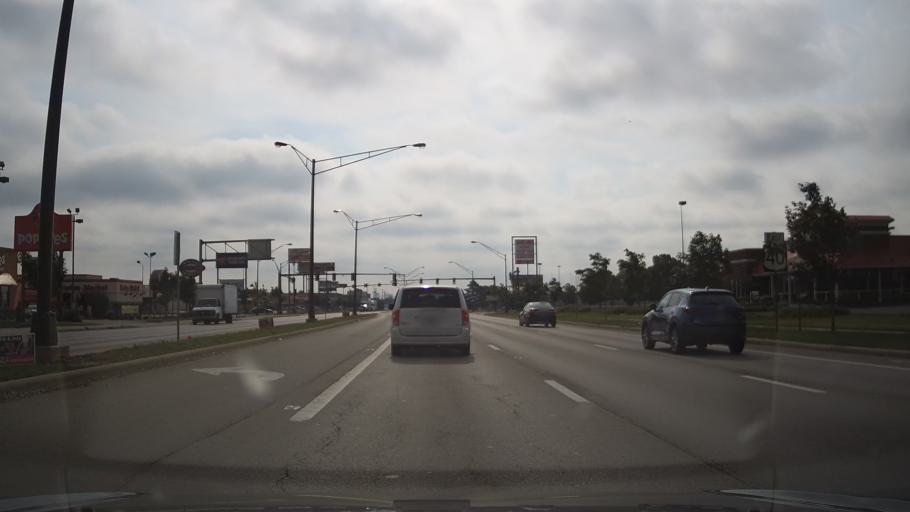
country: US
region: Ohio
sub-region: Franklin County
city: Lincoln Village
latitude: 39.9528
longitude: -83.1173
